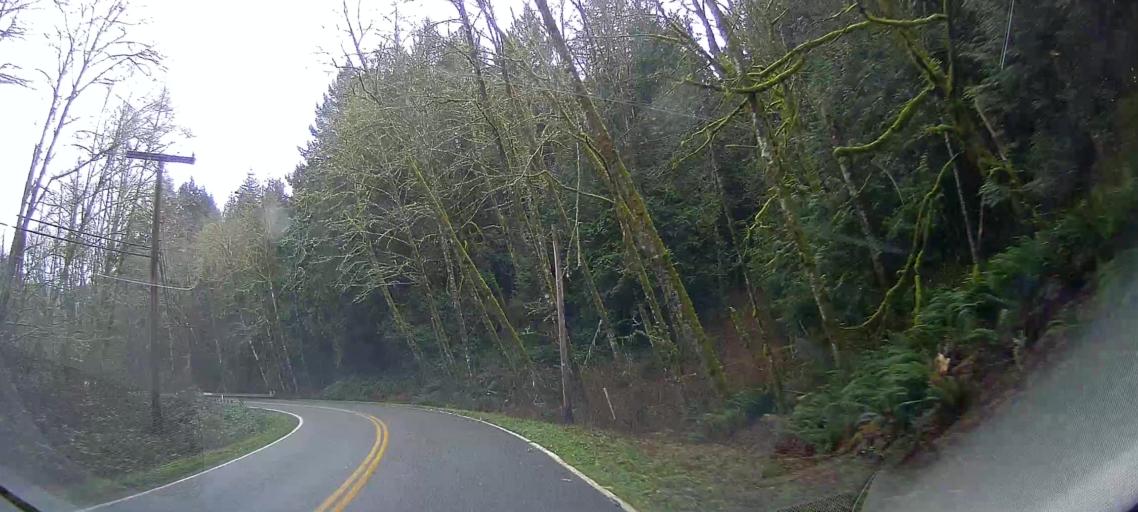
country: US
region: Washington
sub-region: Whatcom County
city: Sudden Valley
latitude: 48.6756
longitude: -122.2899
